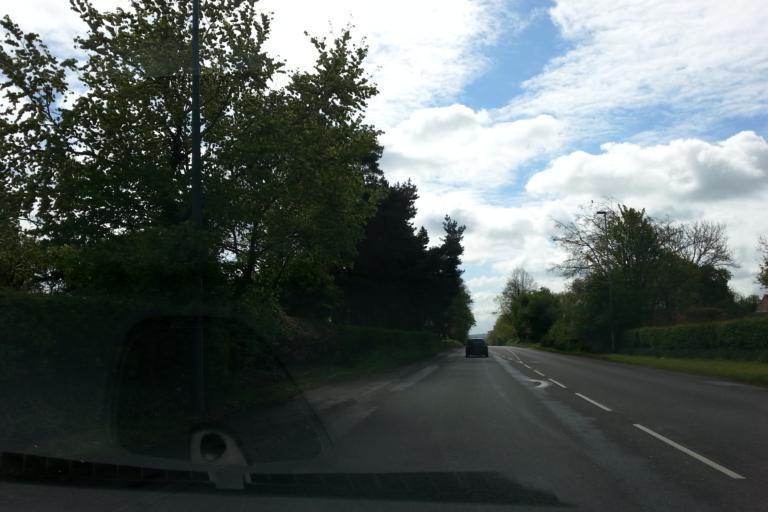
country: GB
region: England
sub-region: Staffordshire
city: Lichfield
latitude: 52.6957
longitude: -1.8520
